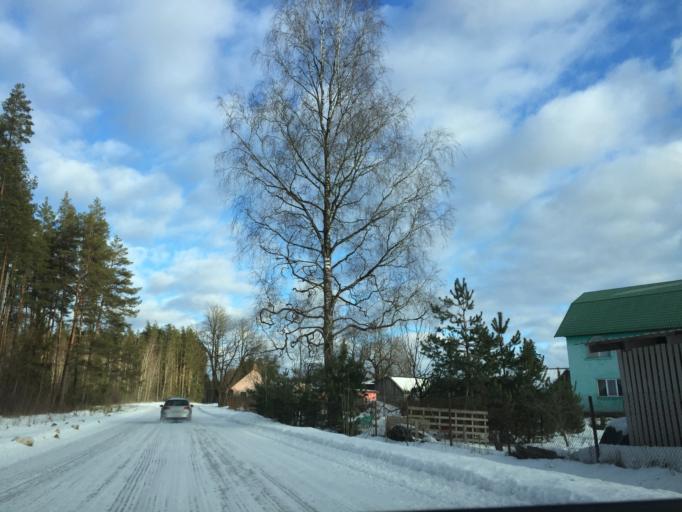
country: LV
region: Ogre
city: Jumprava
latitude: 56.5647
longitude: 24.9219
